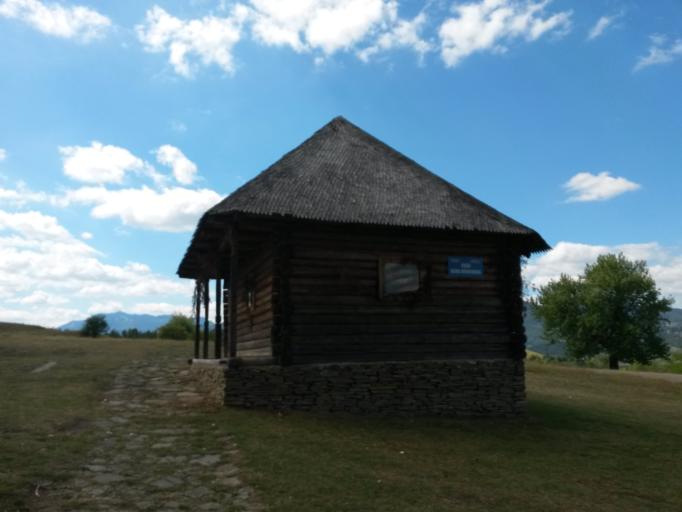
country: RO
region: Vrancea
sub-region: Comuna Barsesti
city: Barsesti
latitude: 45.9109
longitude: 26.7199
